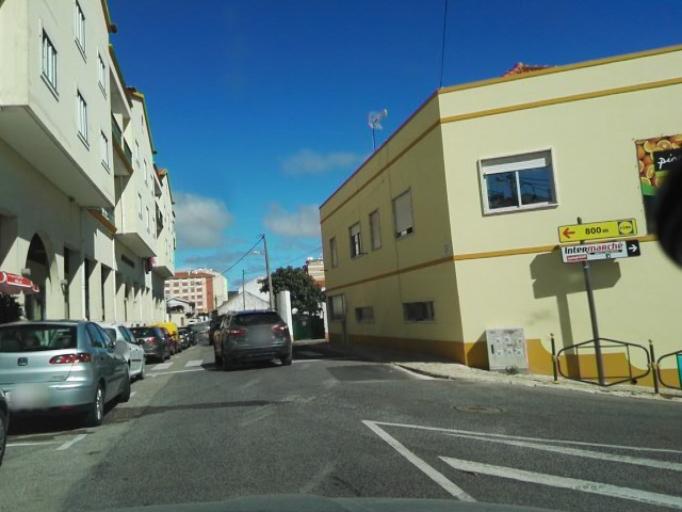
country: PT
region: Lisbon
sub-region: Arruda Dos Vinhos
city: Arruda dos Vinhos
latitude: 38.9859
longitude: -9.0779
